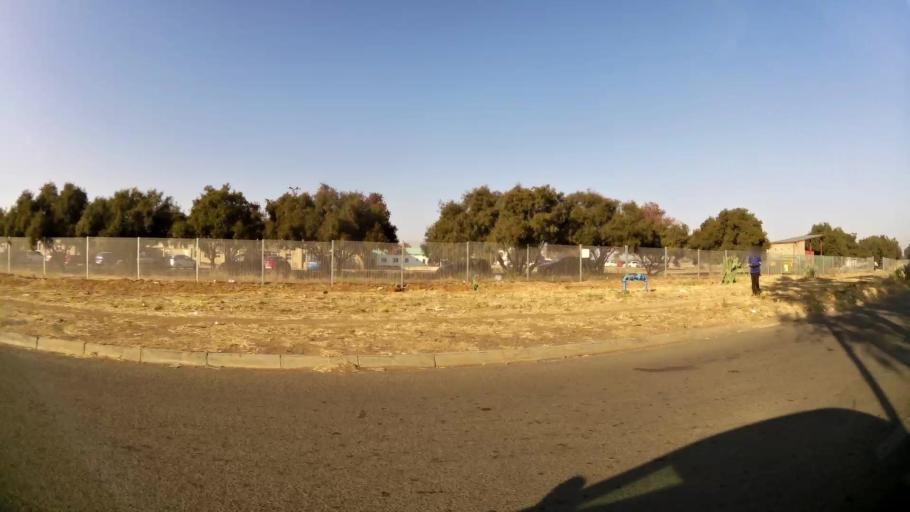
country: ZA
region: Orange Free State
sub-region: Mangaung Metropolitan Municipality
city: Bloemfontein
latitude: -29.1569
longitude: 26.2162
